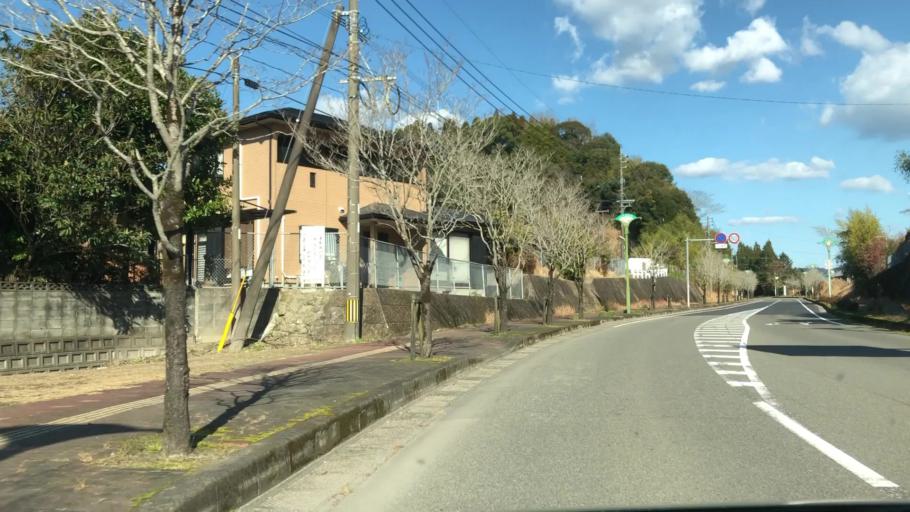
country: JP
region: Kagoshima
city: Satsumasendai
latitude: 31.8239
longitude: 130.4323
